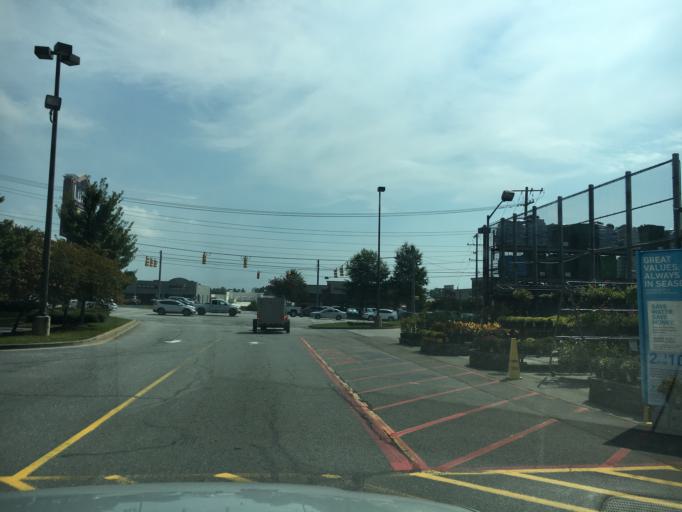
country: US
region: South Carolina
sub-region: Spartanburg County
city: Arcadia
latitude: 34.9343
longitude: -81.9908
